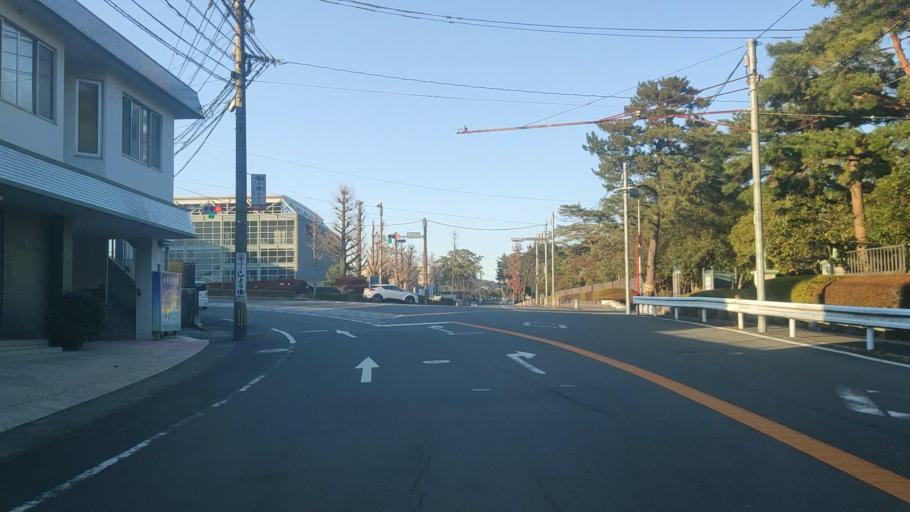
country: JP
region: Oita
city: Beppu
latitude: 33.2812
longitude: 131.4890
